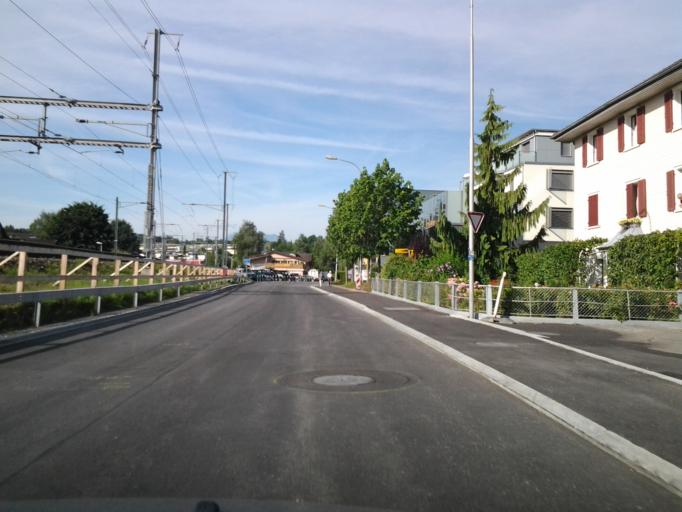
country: CH
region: Zug
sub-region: Zug
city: Cham
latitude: 47.1758
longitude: 8.4516
